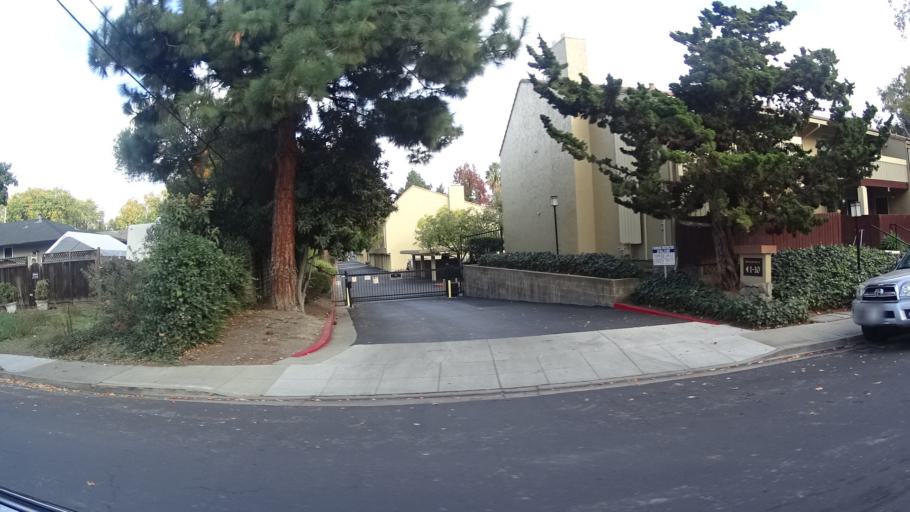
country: US
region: California
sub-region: Santa Clara County
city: Santa Clara
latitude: 37.3359
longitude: -121.9643
